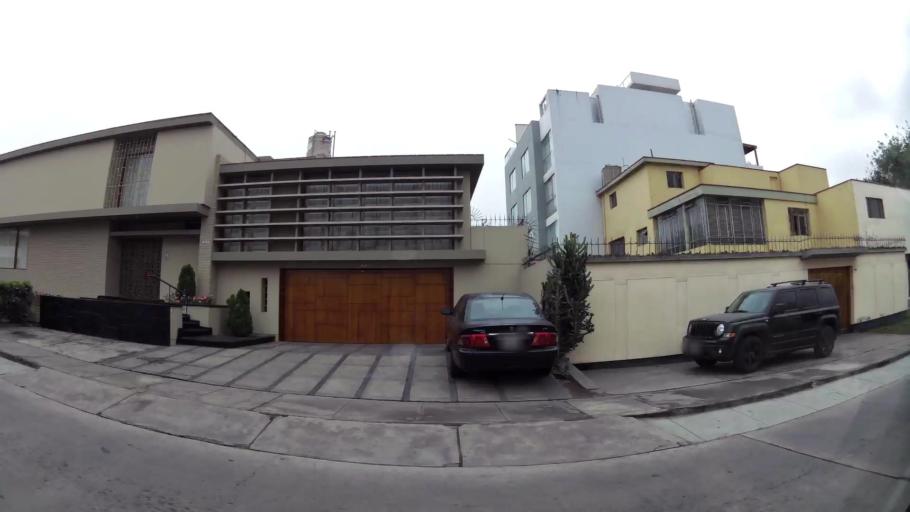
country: PE
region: Lima
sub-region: Lima
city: Surco
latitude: -12.1296
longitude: -77.0170
